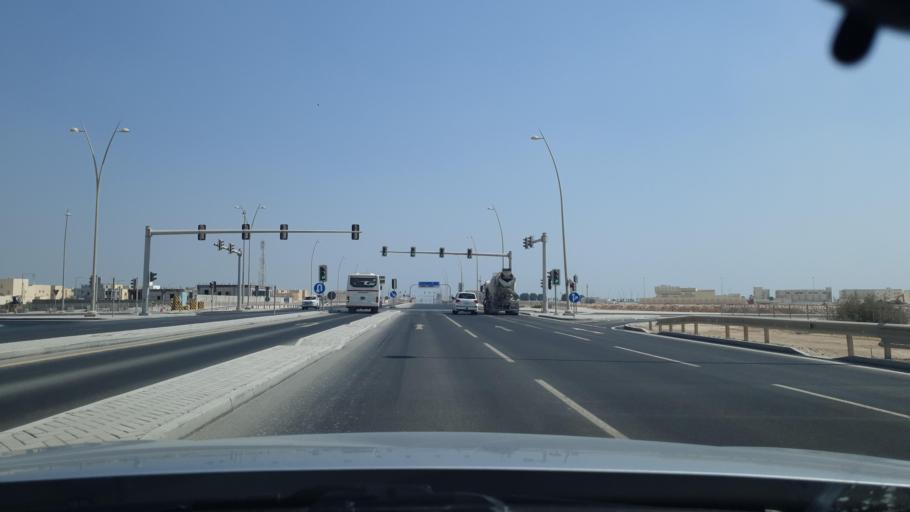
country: QA
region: Al Khawr
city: Al Khawr
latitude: 25.6619
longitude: 51.4918
